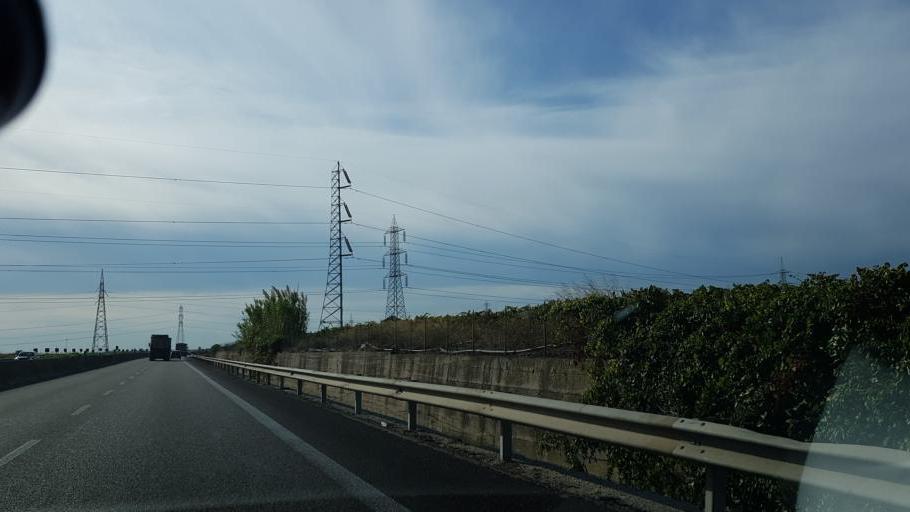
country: IT
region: Apulia
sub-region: Provincia di Brindisi
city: La Rosa
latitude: 40.6089
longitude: 17.9622
